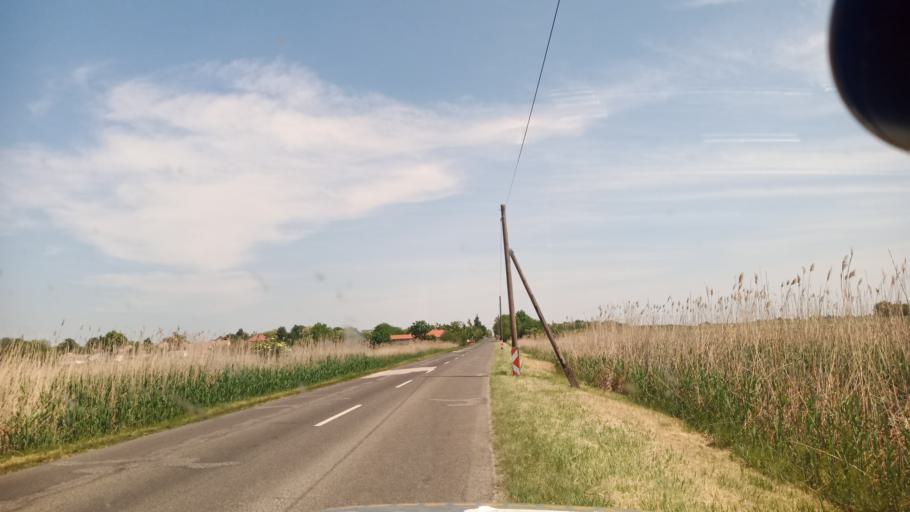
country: HU
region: Bekes
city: Oroshaza
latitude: 46.5672
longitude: 20.5872
